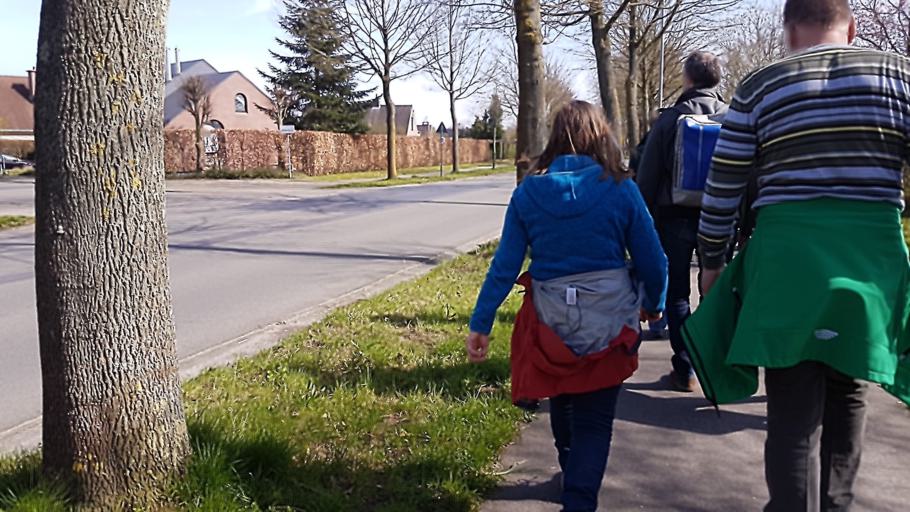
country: BE
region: Flanders
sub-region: Provincie West-Vlaanderen
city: Kortrijk
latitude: 50.8119
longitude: 3.2918
